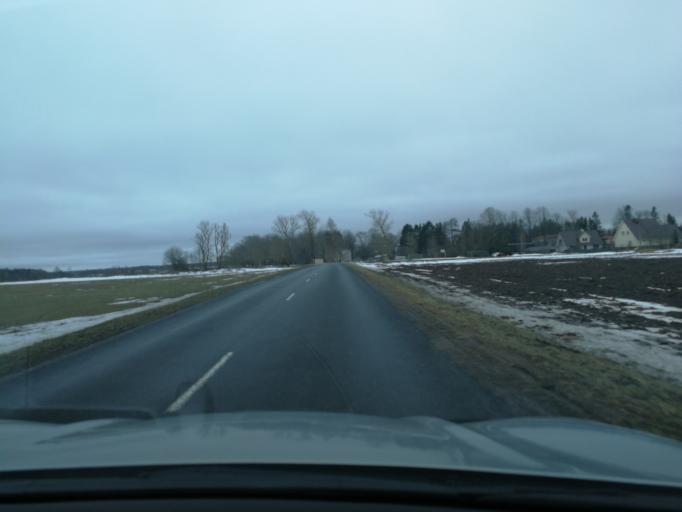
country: EE
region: Harju
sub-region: Kiili vald
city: Kiili
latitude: 59.2771
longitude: 24.8747
